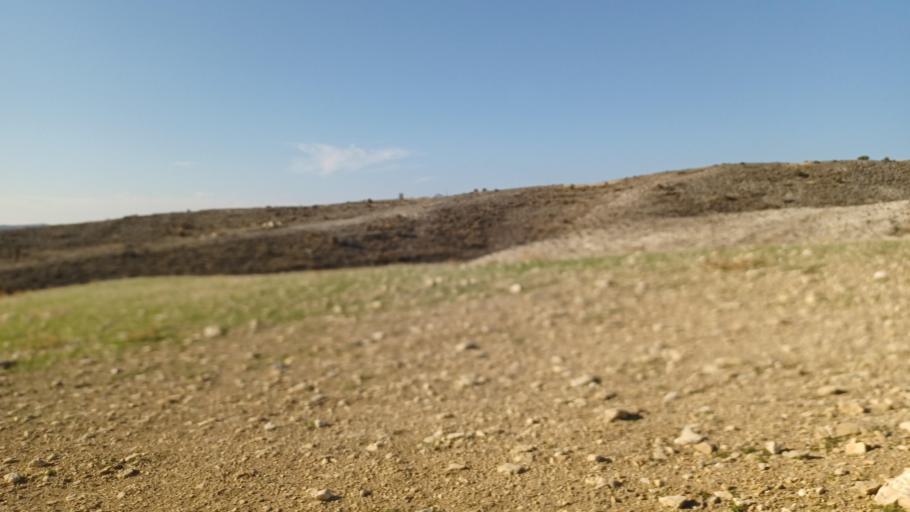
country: CY
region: Larnaka
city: Psevdas
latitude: 34.9446
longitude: 33.5186
